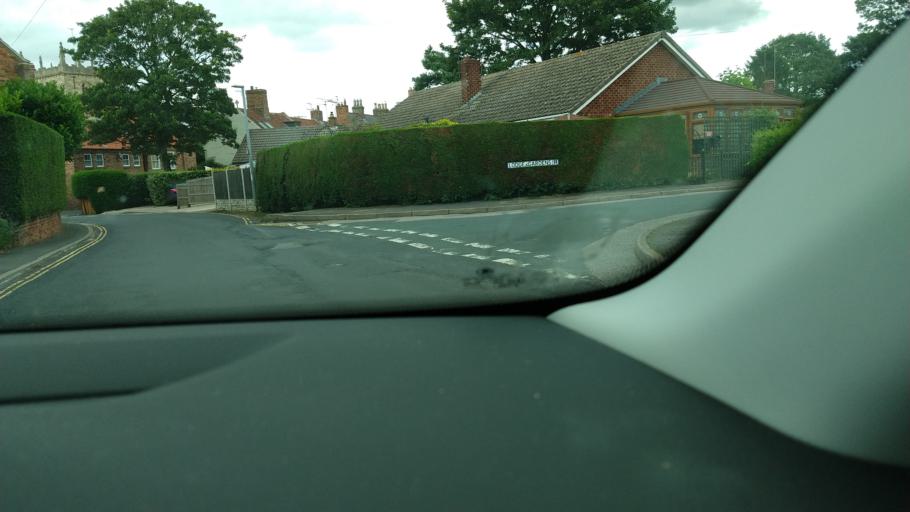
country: GB
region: England
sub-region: East Riding of Yorkshire
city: Snaith
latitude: 53.6911
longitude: -1.0320
